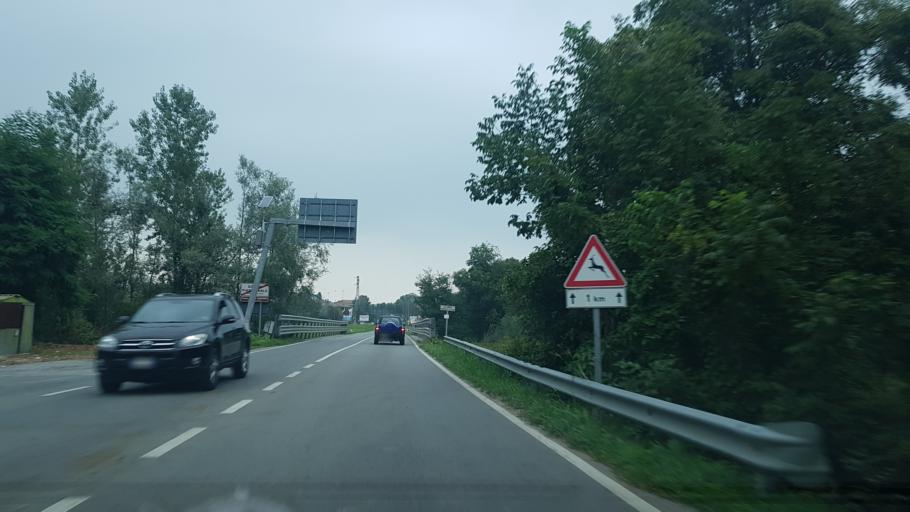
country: IT
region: Piedmont
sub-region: Provincia di Cuneo
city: Villanova Mondovi
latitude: 44.3406
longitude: 7.7779
